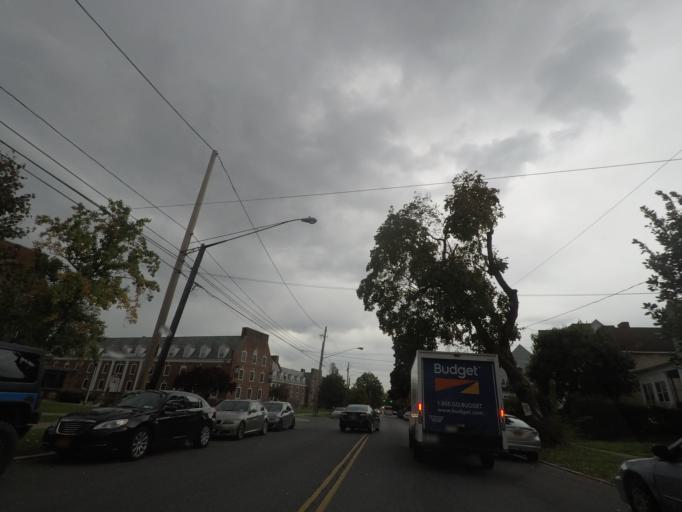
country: US
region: New York
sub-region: Albany County
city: West Albany
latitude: 42.6632
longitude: -73.7816
